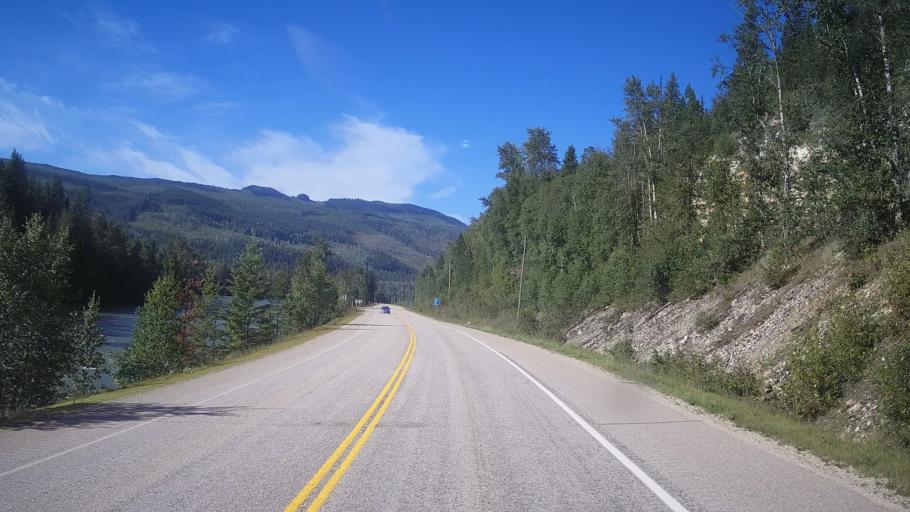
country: CA
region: British Columbia
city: Chase
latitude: 51.6902
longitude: -119.4172
